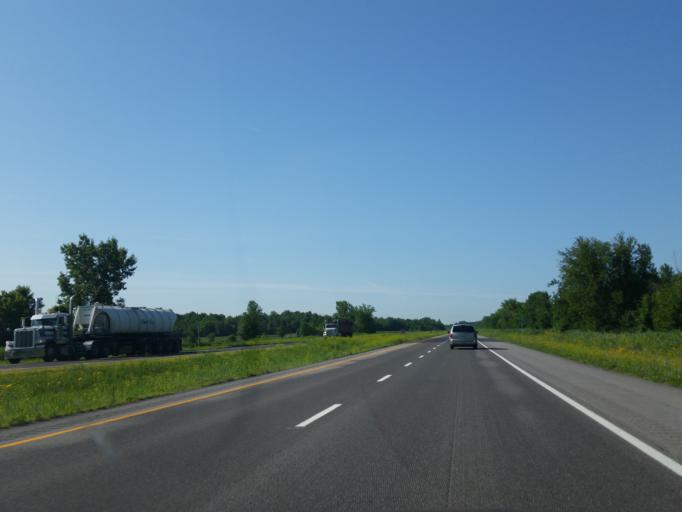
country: CA
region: Quebec
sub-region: Monteregie
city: Napierville
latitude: 45.2346
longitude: -73.4747
